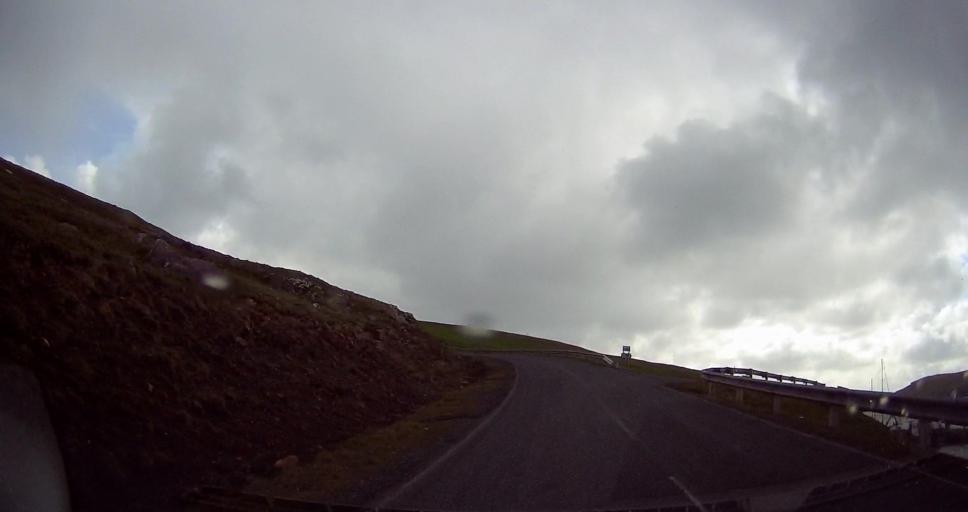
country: GB
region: Scotland
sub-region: Shetland Islands
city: Lerwick
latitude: 60.5414
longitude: -1.3517
